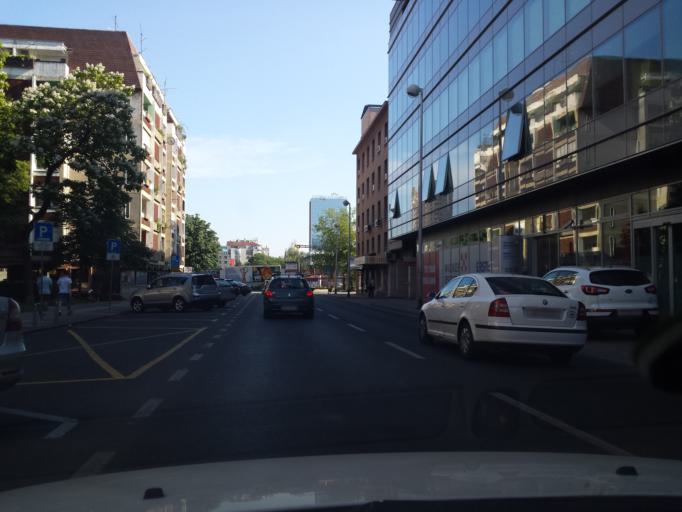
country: HR
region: Grad Zagreb
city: Zagreb - Centar
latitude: 45.8104
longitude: 15.9524
